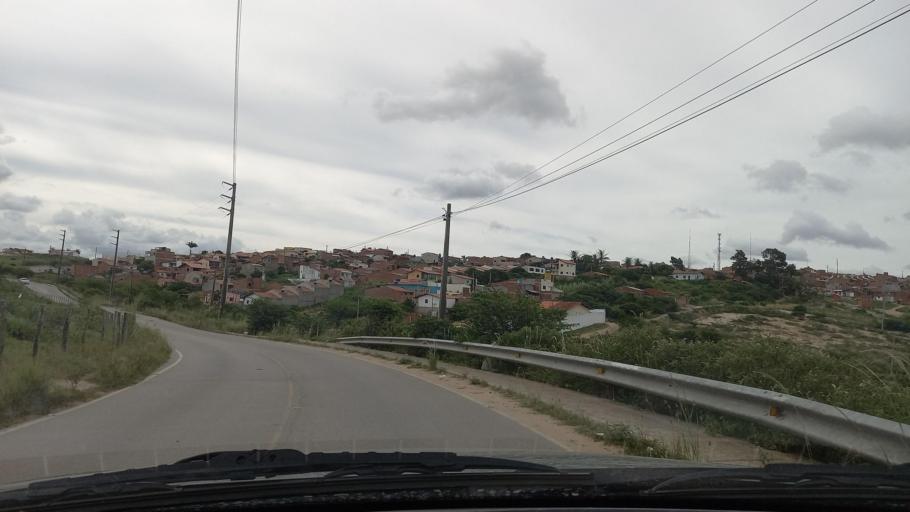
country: BR
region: Pernambuco
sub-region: Gravata
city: Gravata
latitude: -8.2188
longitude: -35.5764
